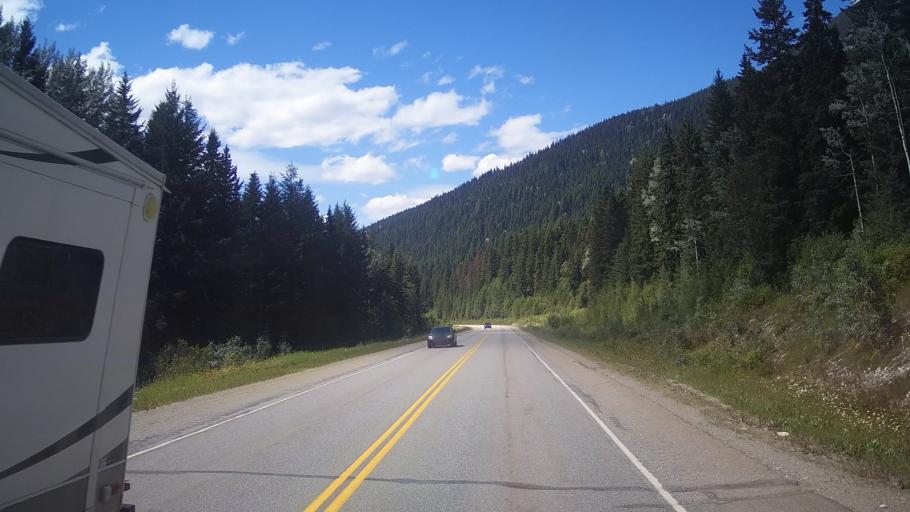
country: CA
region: Alberta
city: Grande Cache
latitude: 53.0190
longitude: -119.0949
